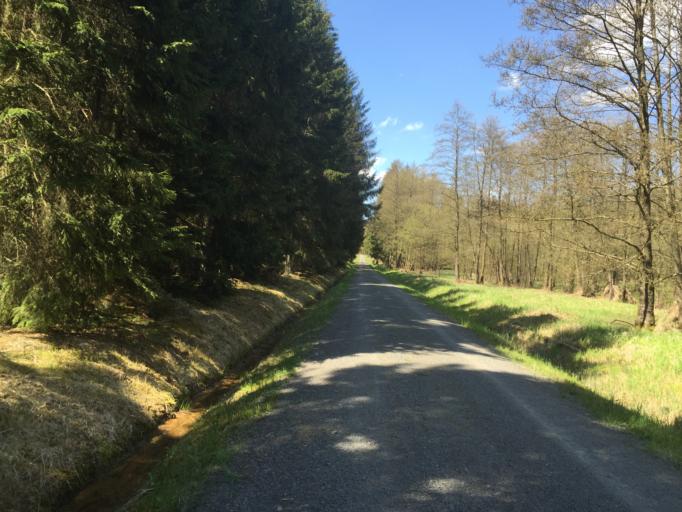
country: DE
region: Bavaria
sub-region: Regierungsbezirk Unterfranken
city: Sulzfeld
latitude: 50.2310
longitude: 10.4368
